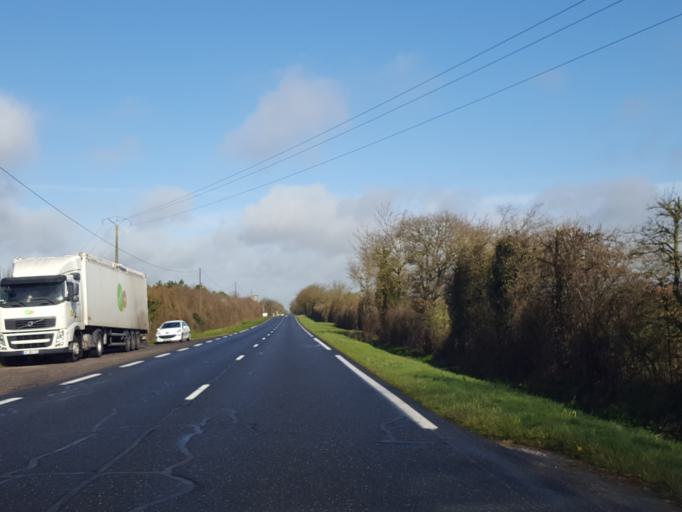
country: FR
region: Pays de la Loire
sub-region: Departement de la Vendee
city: Saligny
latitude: 46.8119
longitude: -1.4609
